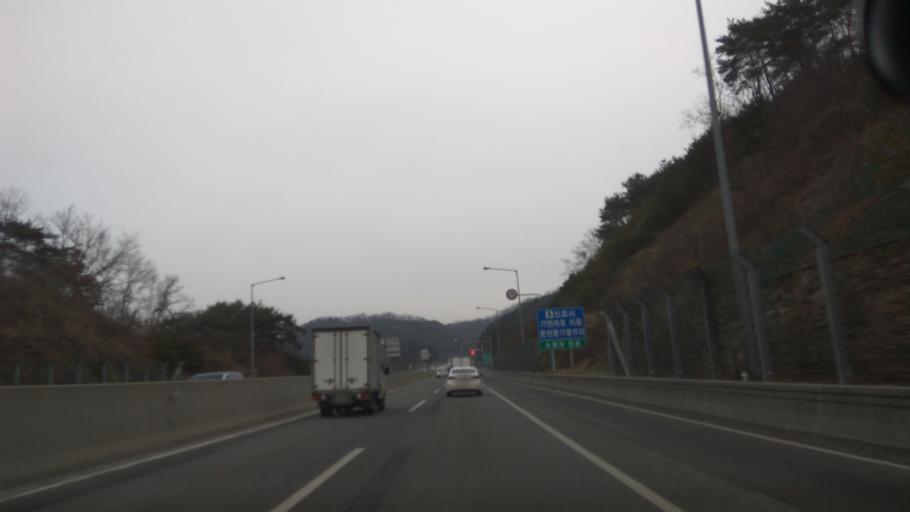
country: KR
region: Gangwon-do
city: Sindong
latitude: 37.7362
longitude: 127.6286
